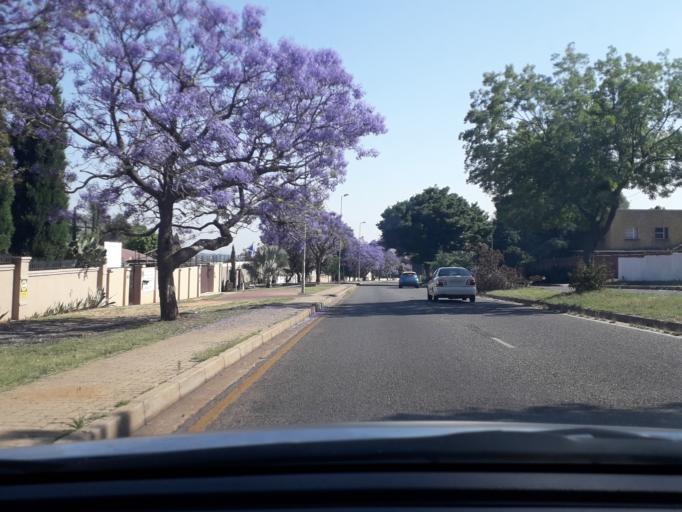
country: ZA
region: Gauteng
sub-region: City of Johannesburg Metropolitan Municipality
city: Roodepoort
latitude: -26.1134
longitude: 27.9725
